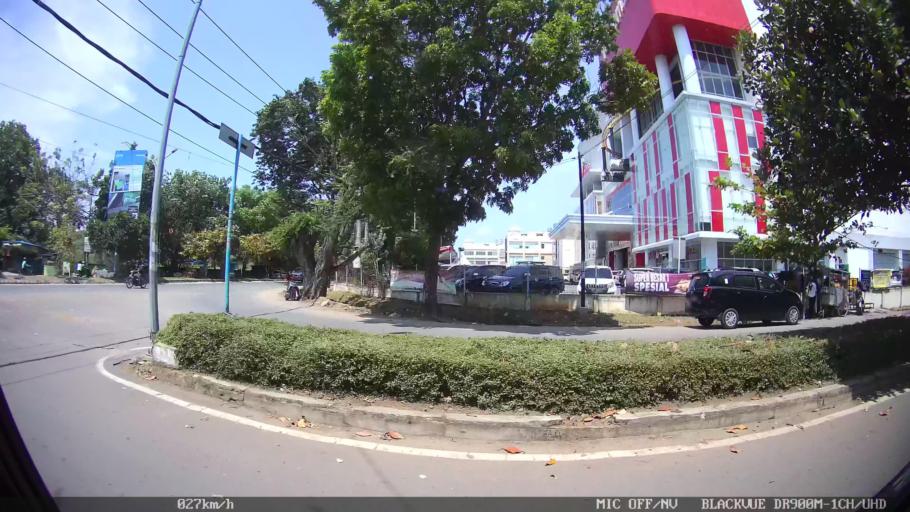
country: ID
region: Lampung
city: Kedaton
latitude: -5.3832
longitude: 105.2821
